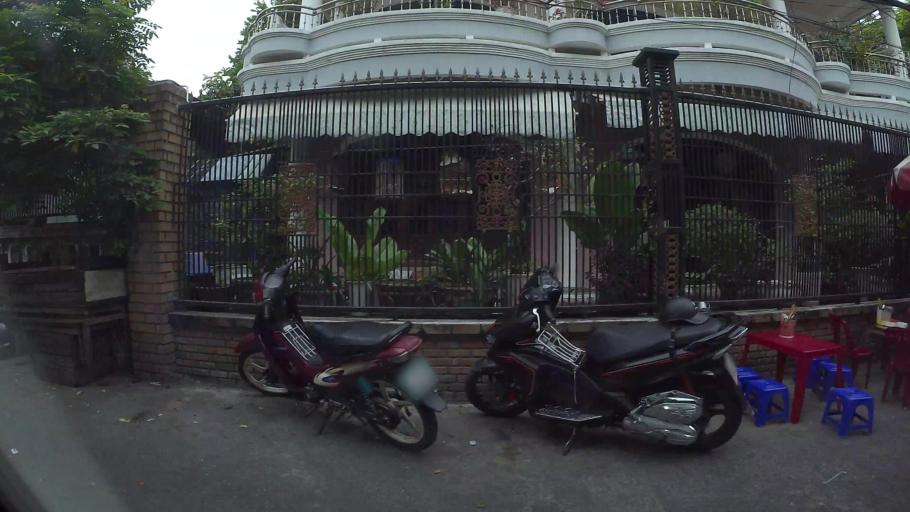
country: VN
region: Da Nang
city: Thanh Khe
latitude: 16.0648
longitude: 108.1864
